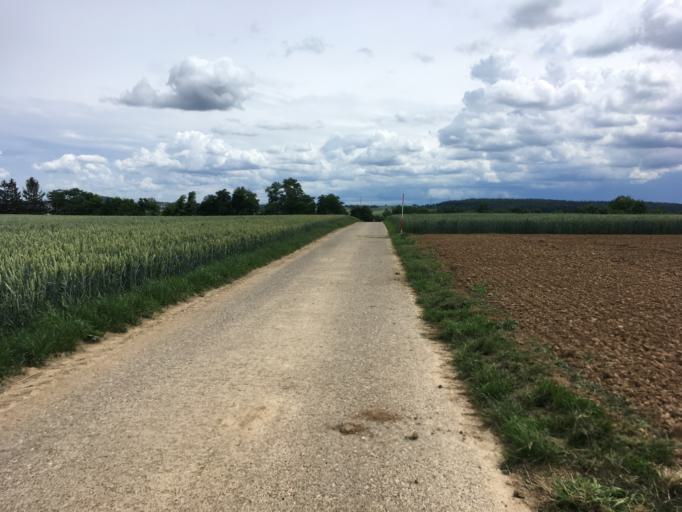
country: DE
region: Baden-Wuerttemberg
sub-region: Regierungsbezirk Stuttgart
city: Bietigheim-Bissingen
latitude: 48.9521
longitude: 9.0942
